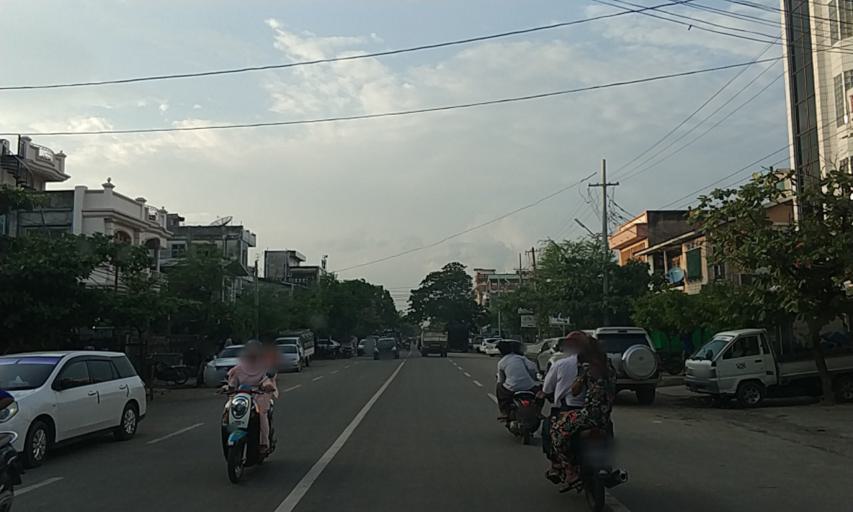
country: MM
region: Mandalay
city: Mandalay
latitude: 21.9710
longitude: 96.0915
